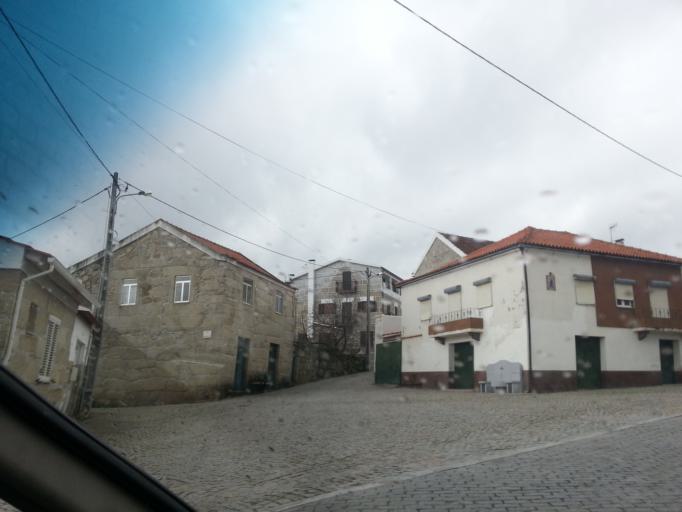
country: PT
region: Guarda
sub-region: Fornos de Algodres
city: Fornos de Algodres
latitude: 40.6166
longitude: -7.5853
